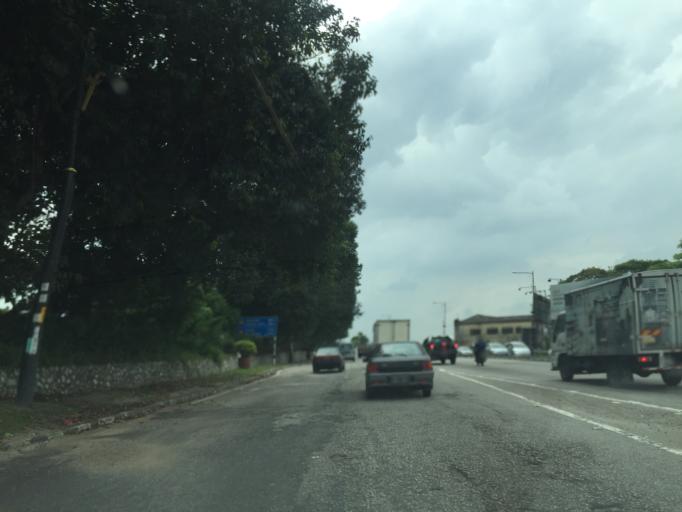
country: MY
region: Selangor
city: Klang
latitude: 3.0348
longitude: 101.4423
